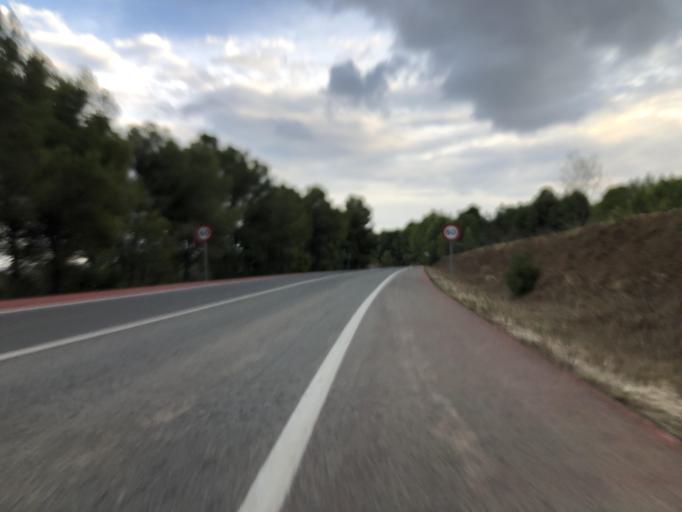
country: ES
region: Valencia
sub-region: Provincia de Alicante
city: Polop
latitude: 38.6344
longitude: -0.1525
